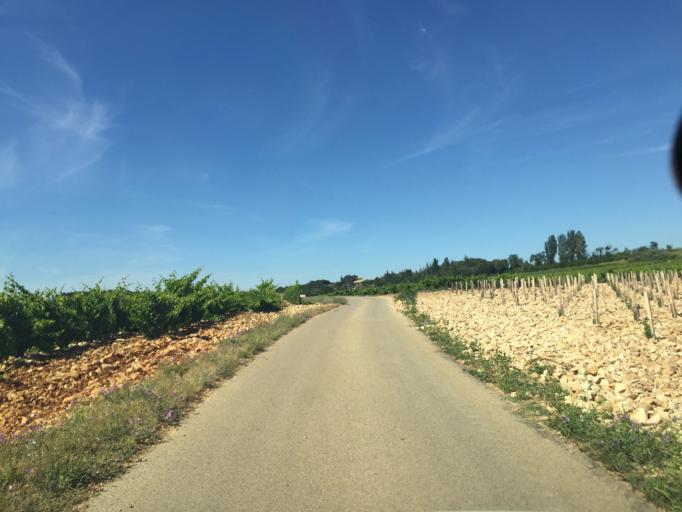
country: FR
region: Provence-Alpes-Cote d'Azur
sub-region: Departement du Vaucluse
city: Chateauneuf-du-Pape
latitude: 44.0761
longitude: 4.8070
